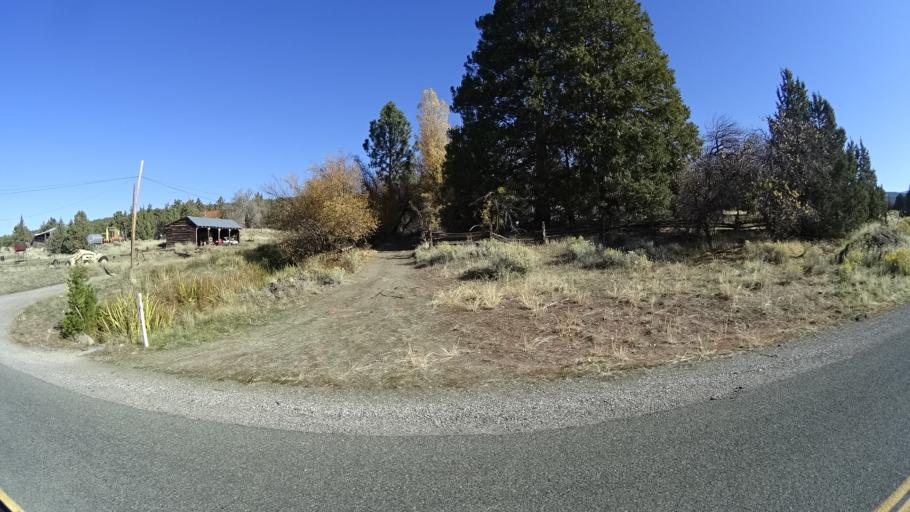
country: US
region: California
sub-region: Siskiyou County
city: Weed
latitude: 41.6223
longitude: -122.3249
